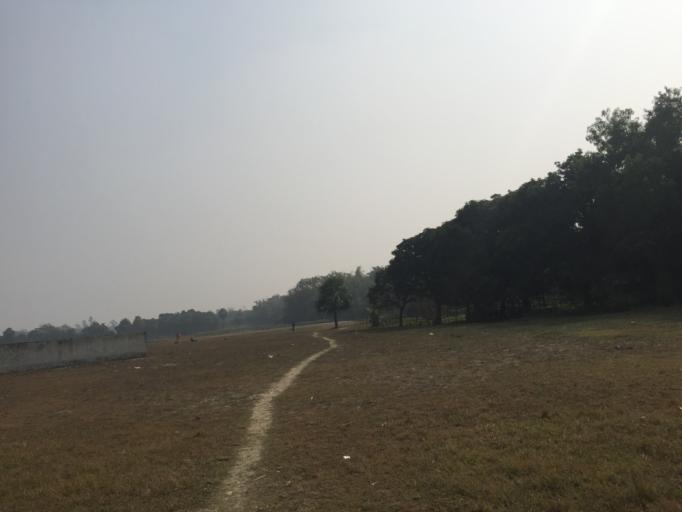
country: BD
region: Dhaka
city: Tungi
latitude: 23.8652
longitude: 90.3149
